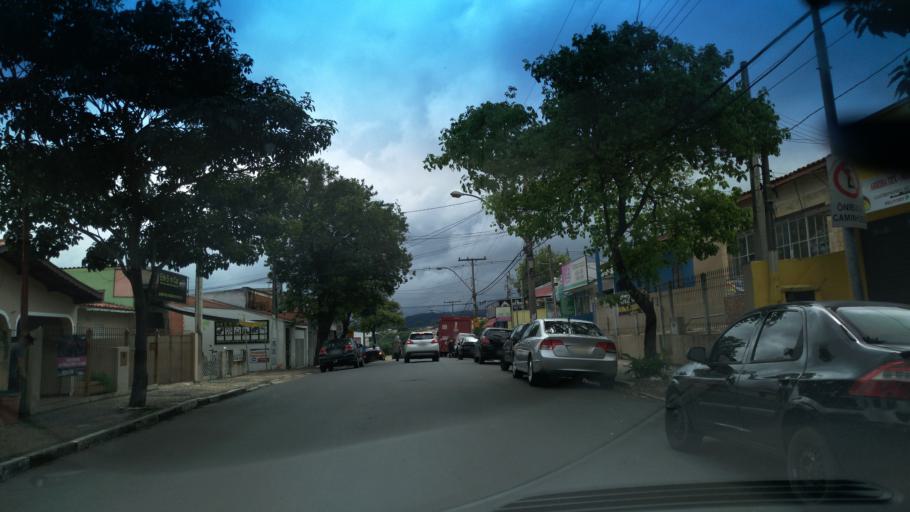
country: BR
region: Sao Paulo
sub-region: Valinhos
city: Valinhos
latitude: -22.9653
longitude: -46.9908
